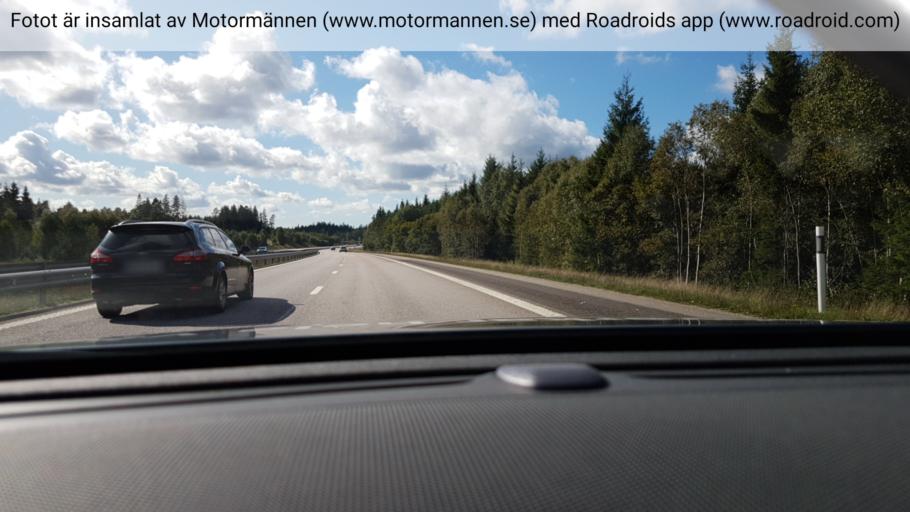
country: SE
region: Vaestra Goetaland
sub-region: Boras Kommun
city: Sandared
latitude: 57.6797
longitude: 12.7045
